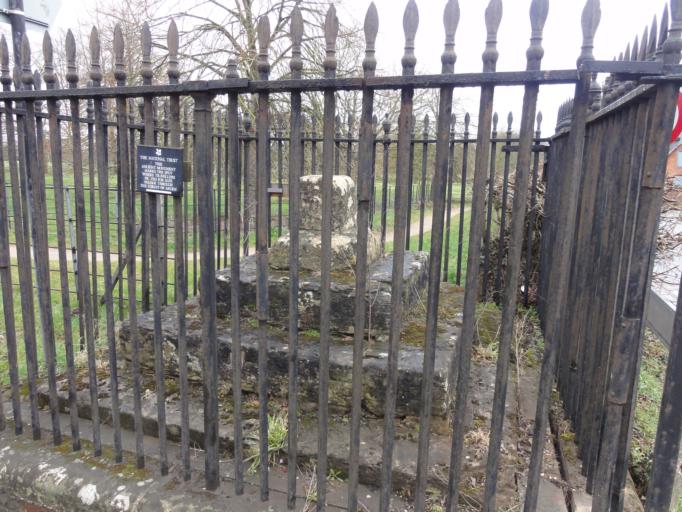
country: GB
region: England
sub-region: Warwickshire
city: Studley
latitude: 52.2415
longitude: -1.8840
